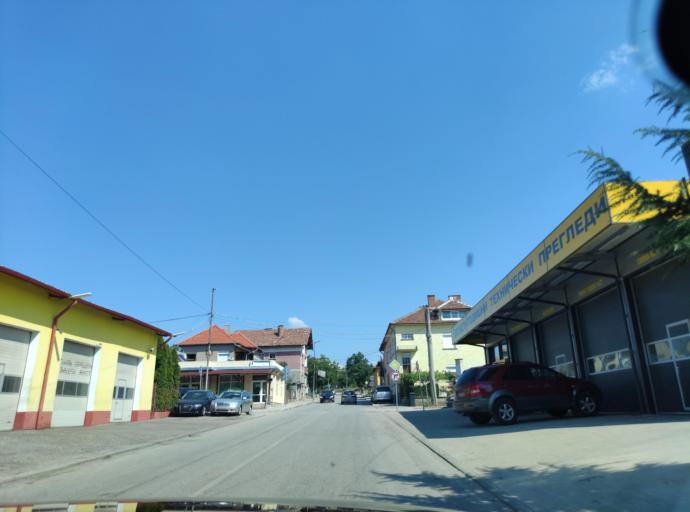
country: BG
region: Pleven
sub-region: Obshtina Cherven Bryag
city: Cherven Bryag
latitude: 43.2769
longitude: 24.0787
